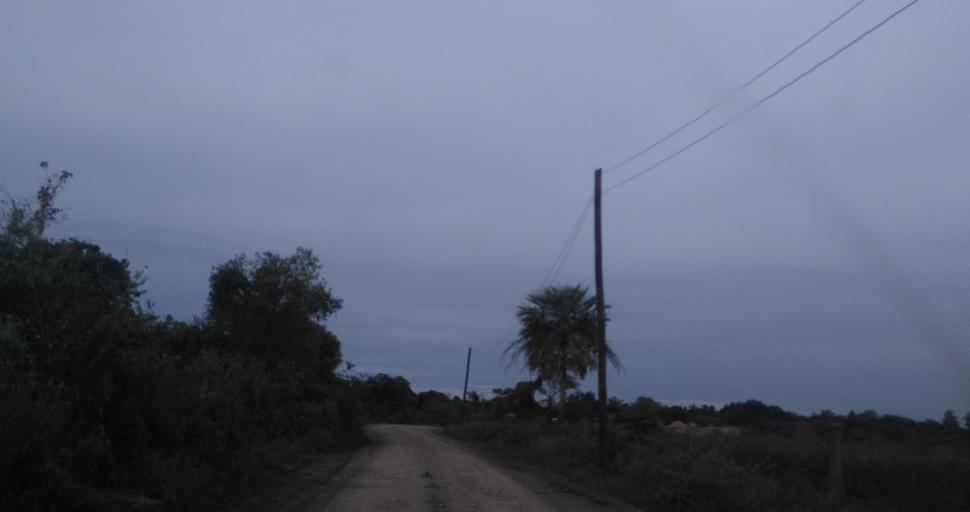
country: AR
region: Chaco
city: Fontana
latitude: -27.4050
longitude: -59.0228
